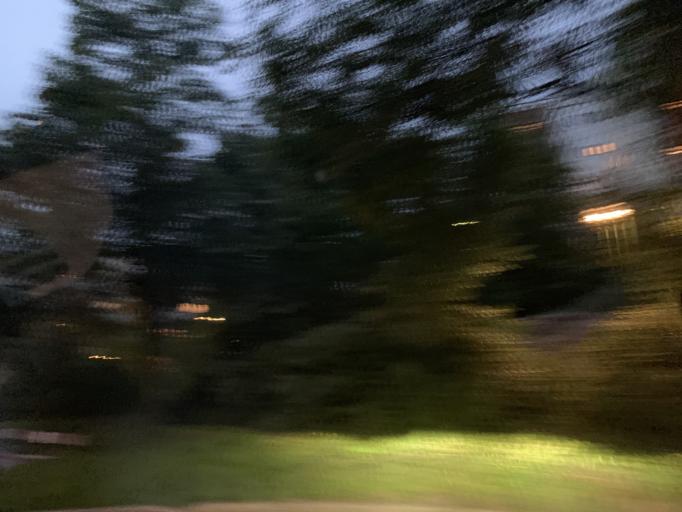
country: SE
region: Stockholm
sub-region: Solna Kommun
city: Solna
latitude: 59.3258
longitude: 18.0147
